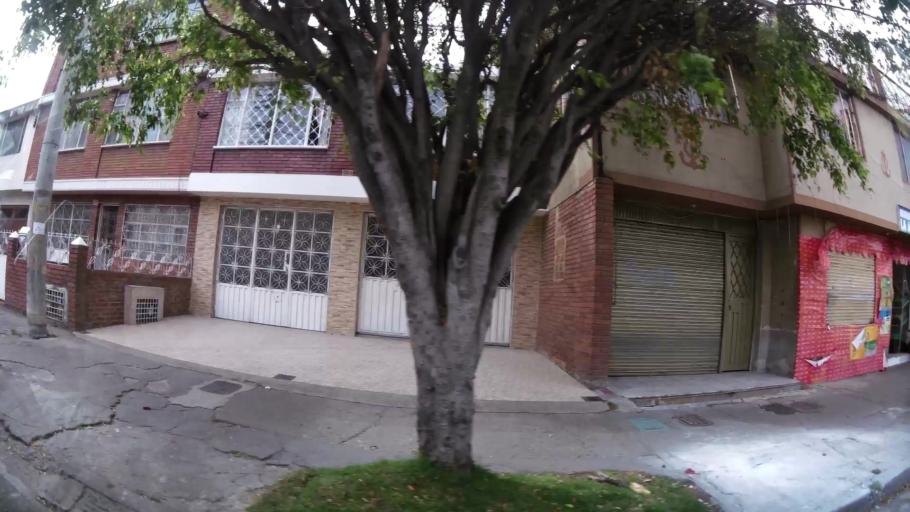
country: CO
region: Bogota D.C.
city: Bogota
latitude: 4.5979
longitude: -74.1328
